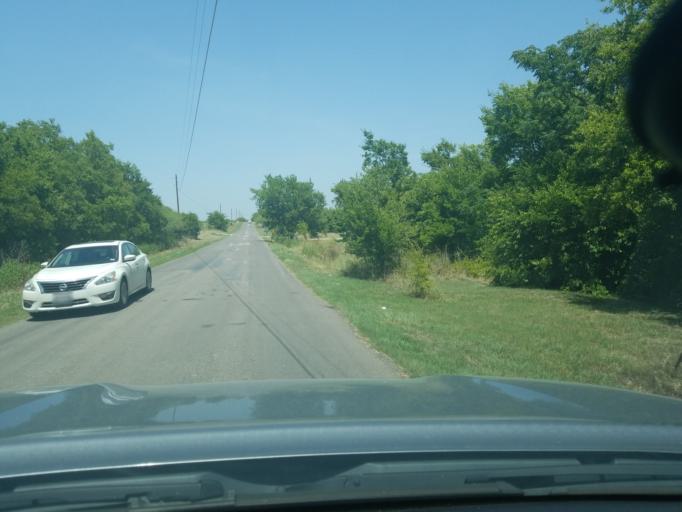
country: US
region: Texas
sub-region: Guadalupe County
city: Cibolo
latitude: 29.5714
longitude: -98.1901
